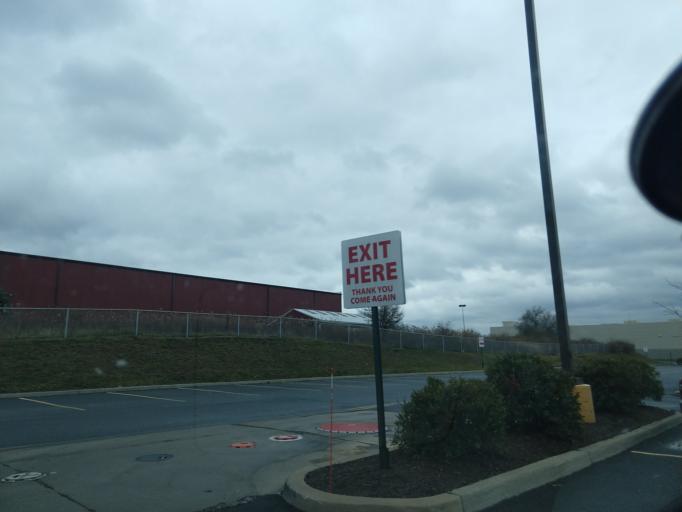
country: US
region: New York
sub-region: Tompkins County
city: Lansing
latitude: 42.4869
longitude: -76.4915
